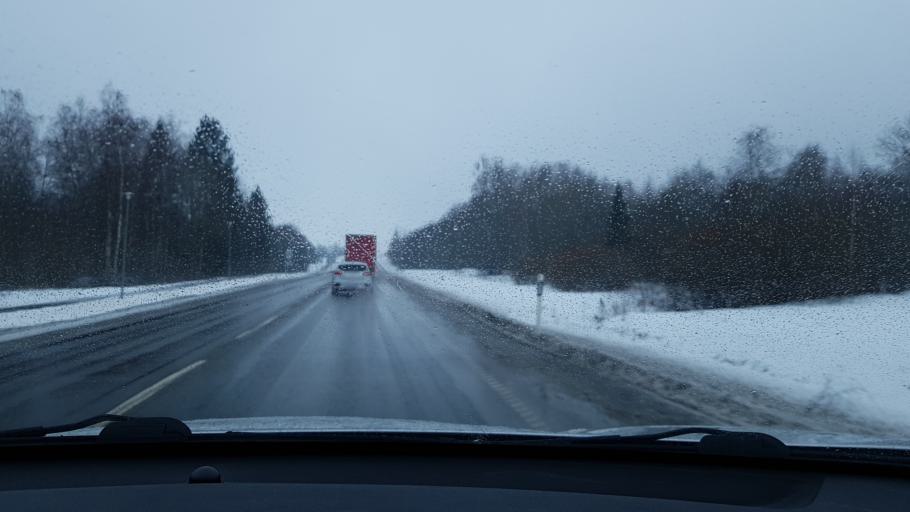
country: EE
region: Jaervamaa
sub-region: Tueri vald
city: Tueri
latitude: 58.8458
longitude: 25.4777
